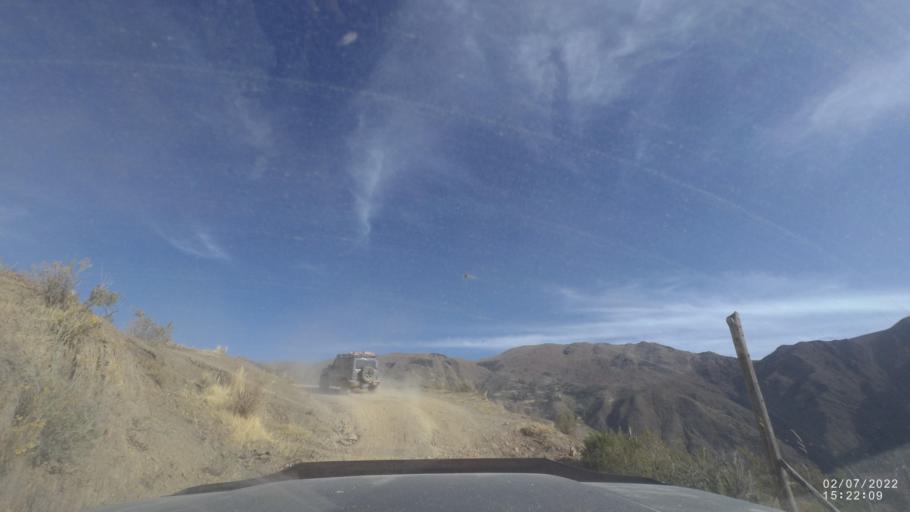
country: BO
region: Cochabamba
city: Irpa Irpa
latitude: -17.8725
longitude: -66.4239
